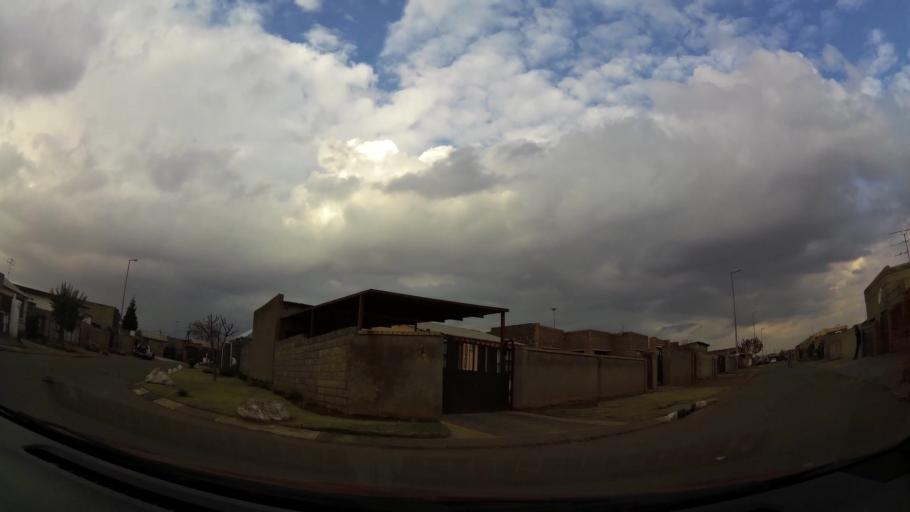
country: ZA
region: Gauteng
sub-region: City of Johannesburg Metropolitan Municipality
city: Soweto
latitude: -26.2374
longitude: 27.8259
